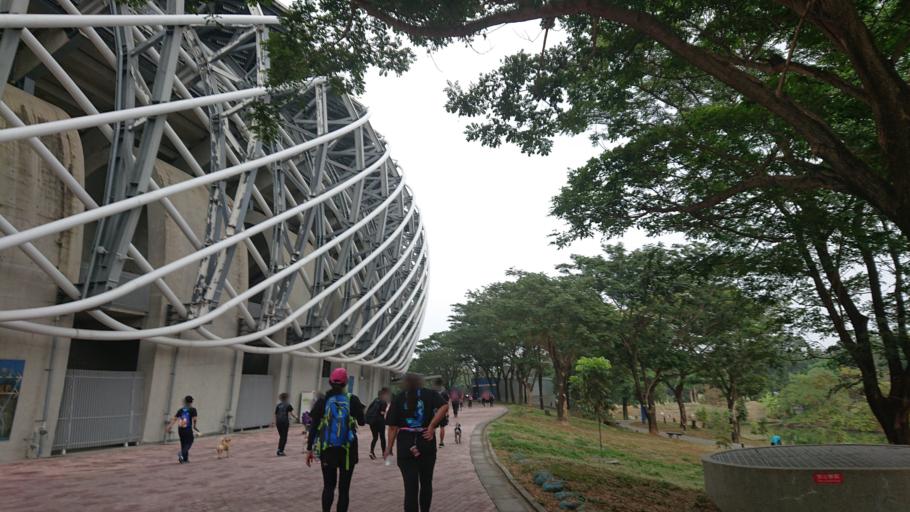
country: TW
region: Kaohsiung
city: Kaohsiung
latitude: 22.7024
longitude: 120.2957
